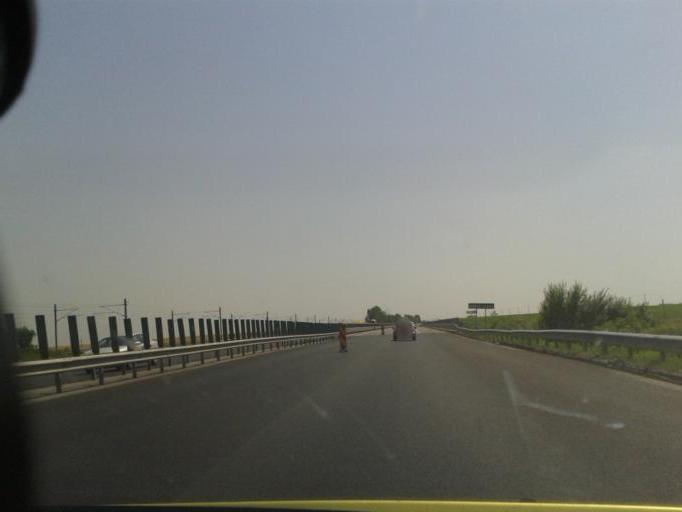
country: RO
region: Calarasi
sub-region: Comuna Tamadau Mare
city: Tamadau Mare
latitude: 44.4468
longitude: 26.5815
